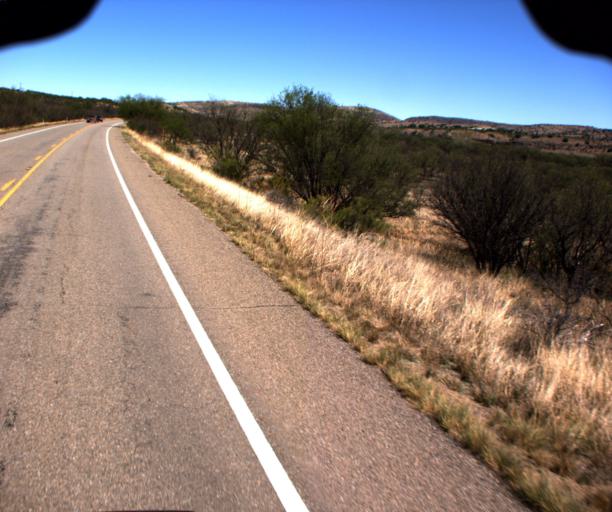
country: US
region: Arizona
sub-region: Santa Cruz County
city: Rio Rico
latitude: 31.6173
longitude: -110.7197
